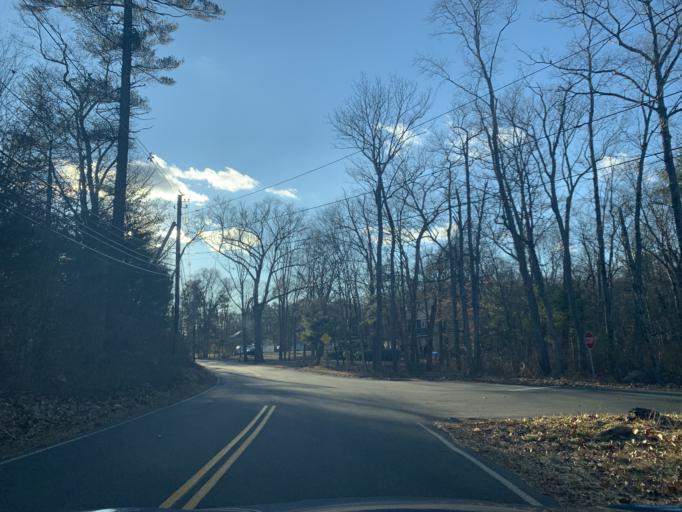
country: US
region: Massachusetts
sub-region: Bristol County
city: Norton
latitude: 41.9558
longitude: -71.1895
